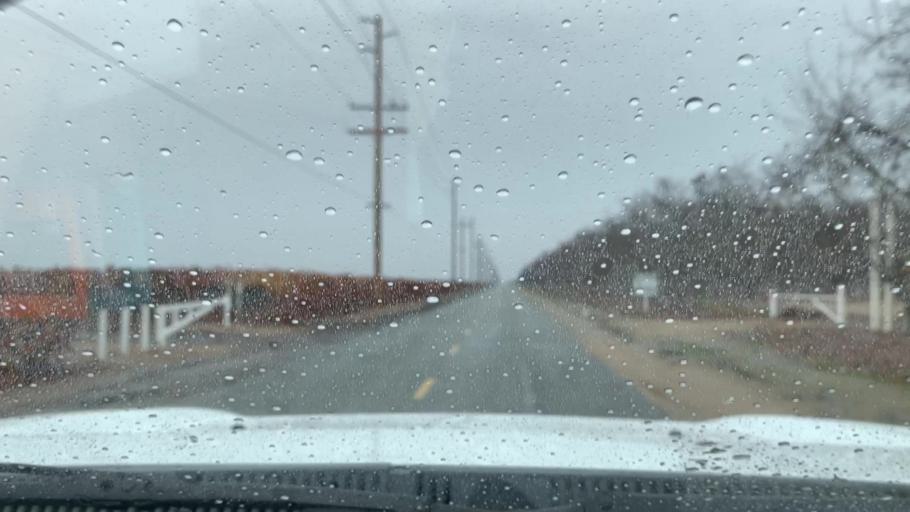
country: US
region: California
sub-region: Tulare County
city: Richgrove
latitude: 35.8341
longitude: -119.1836
